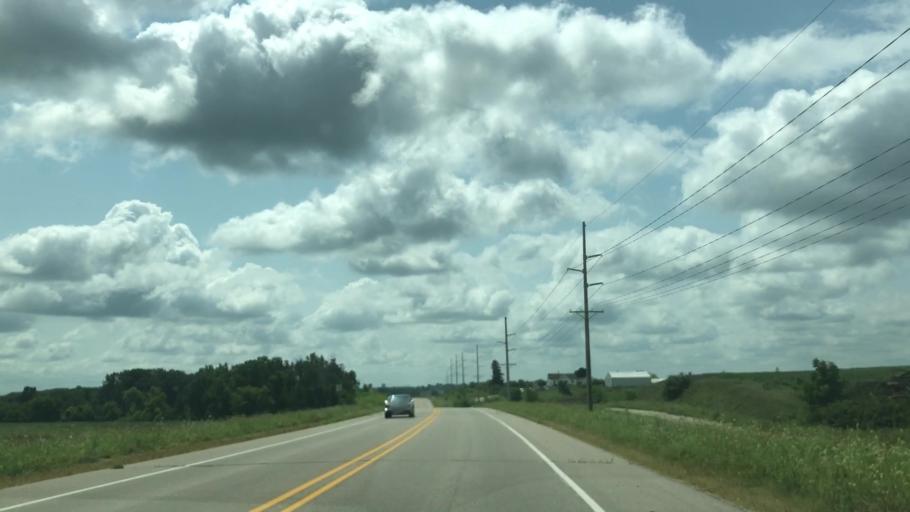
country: US
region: Iowa
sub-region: Marshall County
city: Marshalltown
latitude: 42.0302
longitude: -92.9604
